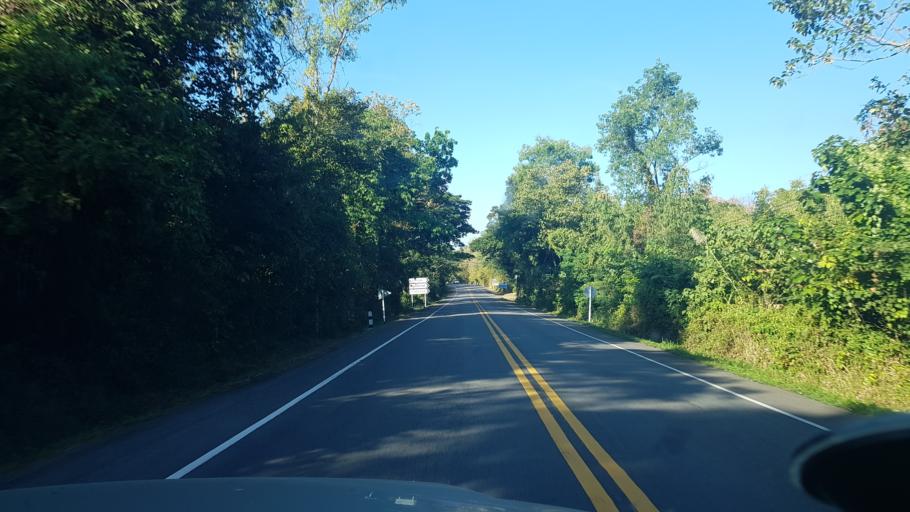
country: TH
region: Phetchabun
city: Nam Nao
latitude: 16.7596
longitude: 101.4700
